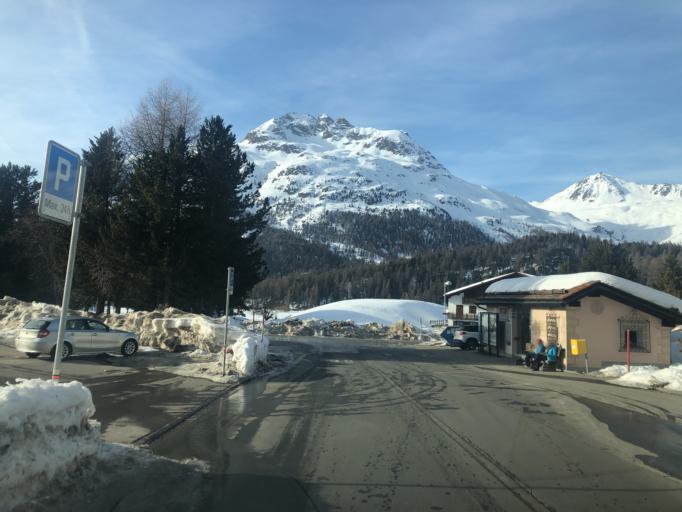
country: CH
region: Grisons
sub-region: Maloja District
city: Silvaplana
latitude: 46.4592
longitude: 9.8118
